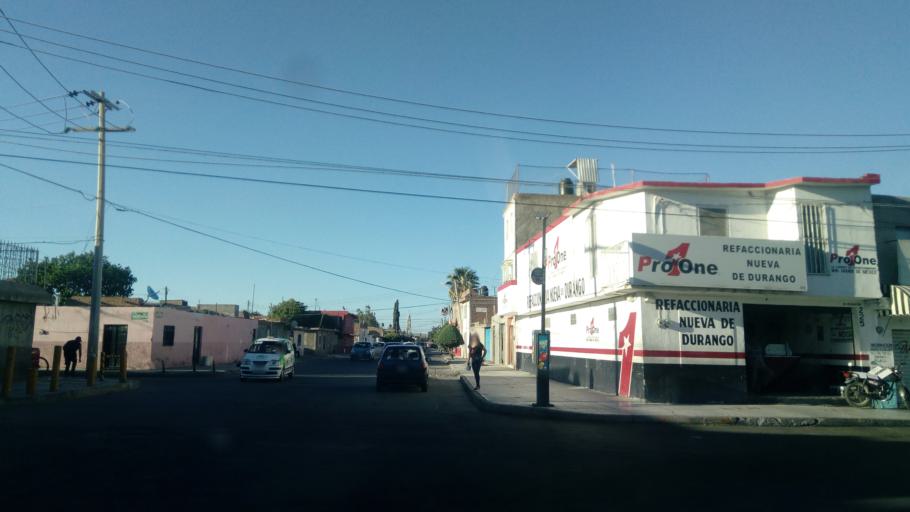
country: MX
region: Durango
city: Victoria de Durango
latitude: 23.9975
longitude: -104.6757
